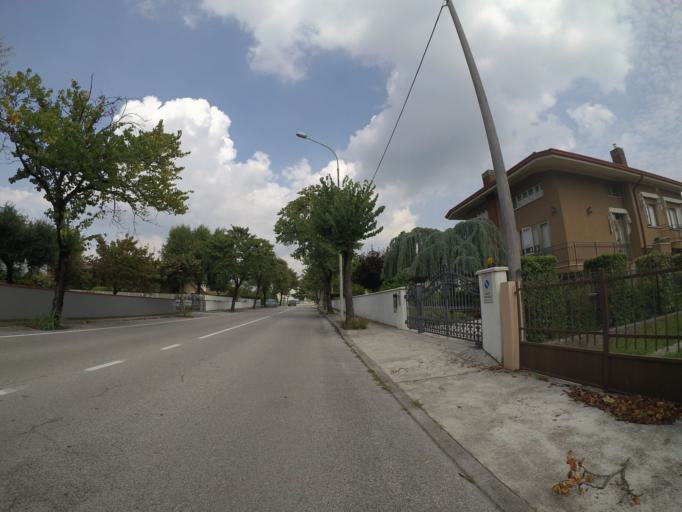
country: IT
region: Friuli Venezia Giulia
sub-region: Provincia di Udine
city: Codroipo
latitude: 45.9605
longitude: 12.9927
